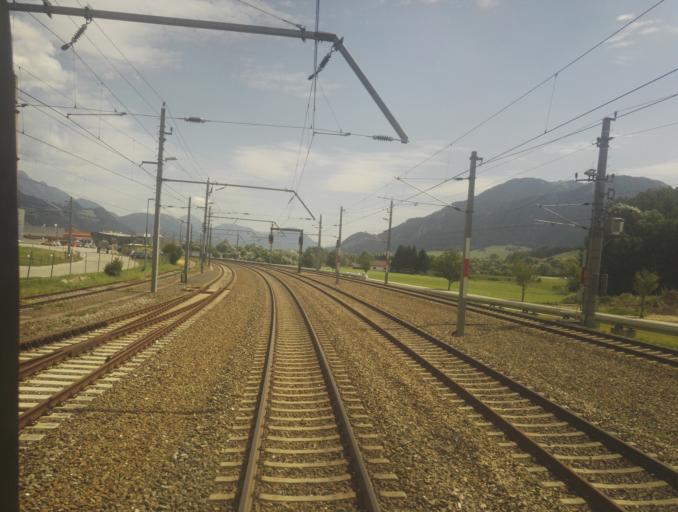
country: AT
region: Styria
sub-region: Politischer Bezirk Liezen
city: Stainach
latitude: 47.5299
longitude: 14.1129
